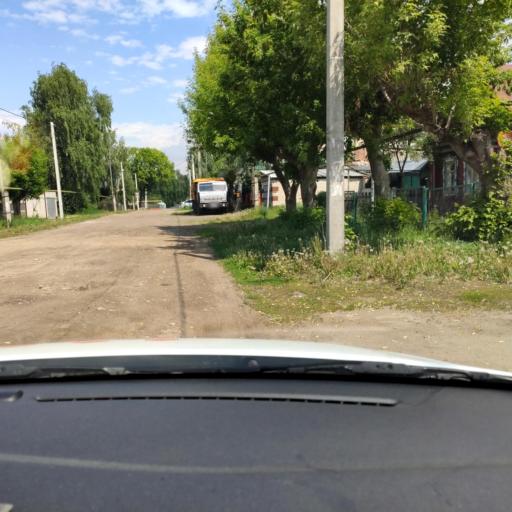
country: RU
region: Tatarstan
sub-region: Gorod Kazan'
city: Kazan
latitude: 55.7132
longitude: 49.0981
